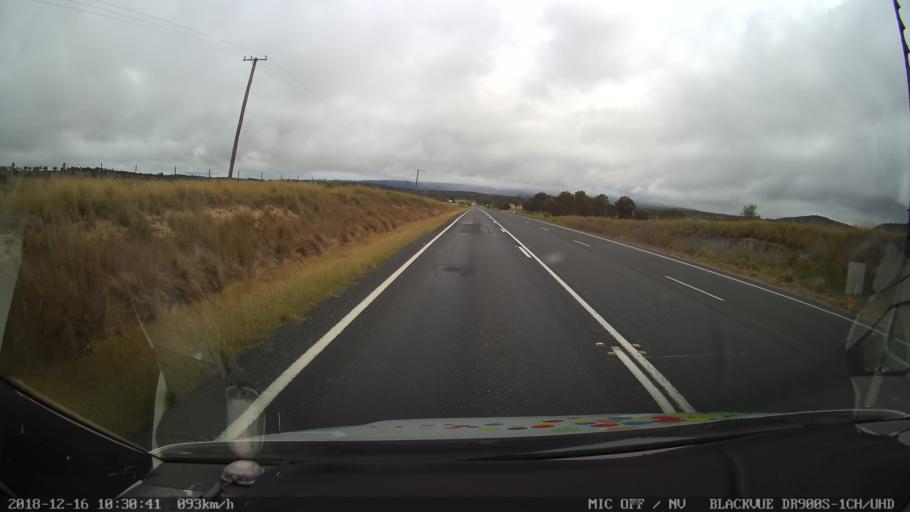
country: AU
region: New South Wales
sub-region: Tenterfield Municipality
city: Carrolls Creek
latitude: -29.0898
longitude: 152.0032
